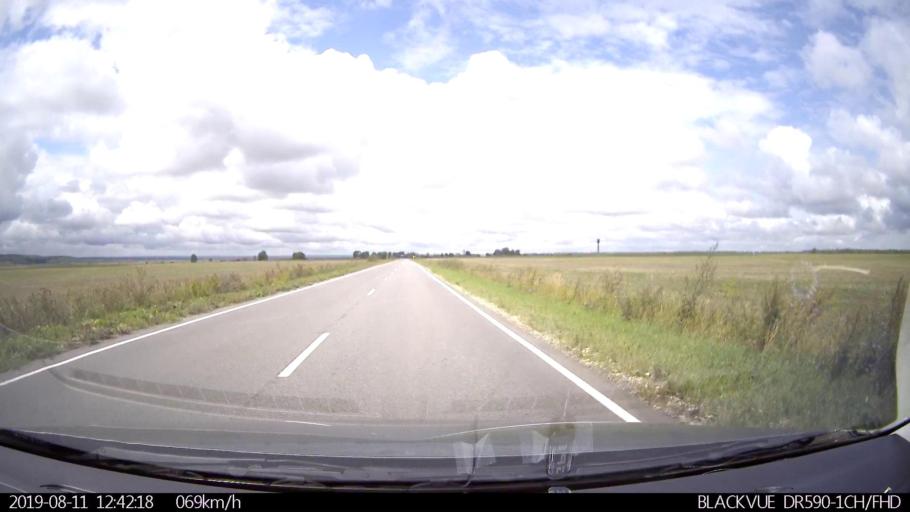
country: RU
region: Ulyanovsk
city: Ignatovka
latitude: 53.8448
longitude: 47.7531
